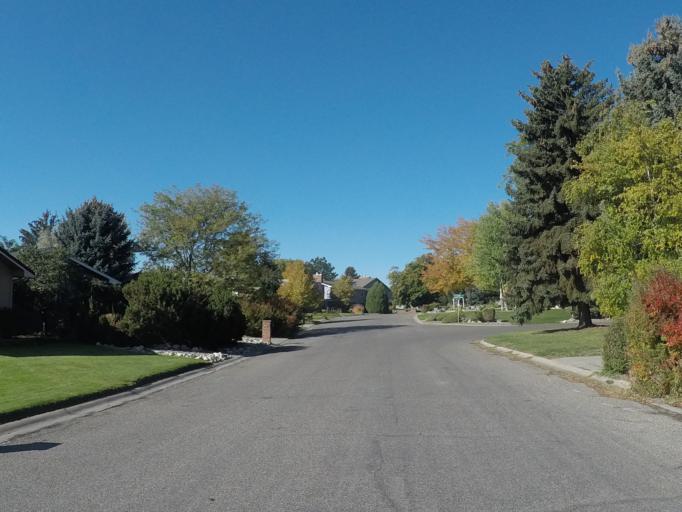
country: US
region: Montana
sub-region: Yellowstone County
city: Billings
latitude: 45.7993
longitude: -108.5930
